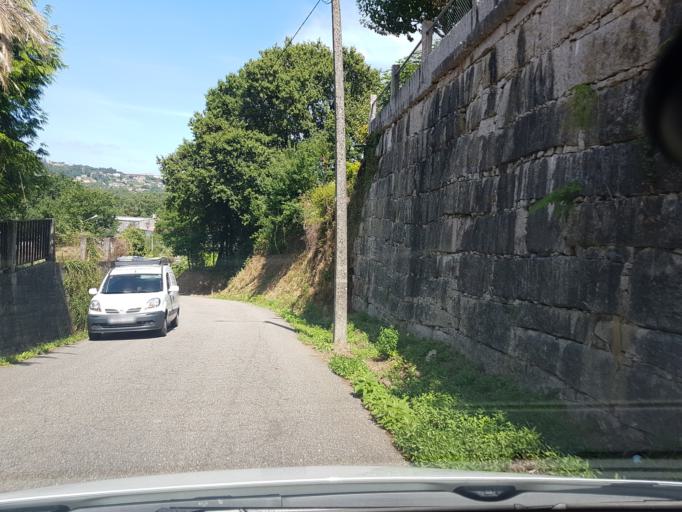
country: ES
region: Galicia
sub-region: Provincia de Pontevedra
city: Porrino
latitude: 42.1995
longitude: -8.6202
